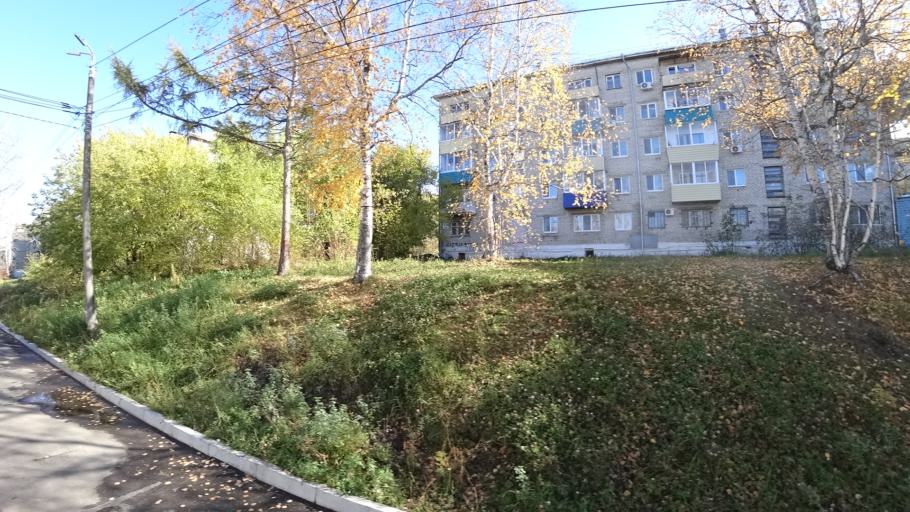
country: RU
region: Khabarovsk Krai
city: Amursk
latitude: 50.2219
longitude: 136.9040
